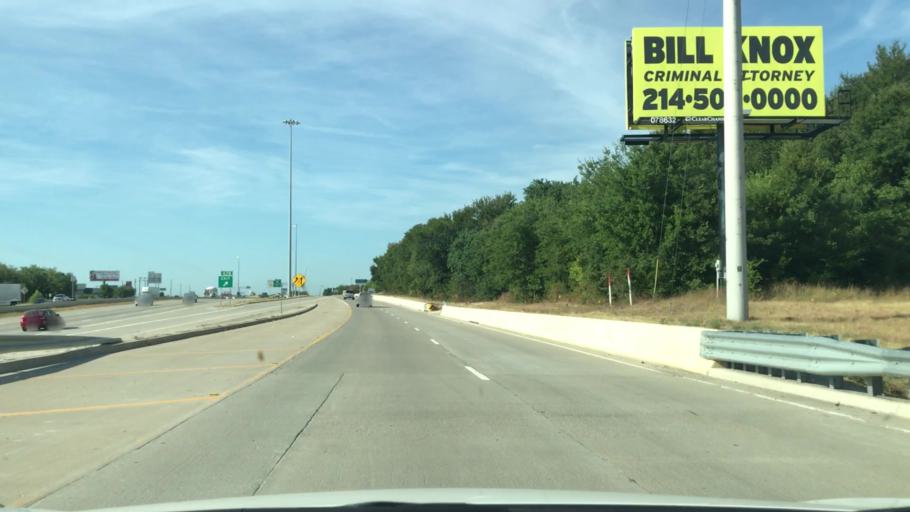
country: US
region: Texas
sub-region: Collin County
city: McKinney
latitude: 33.2384
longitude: -96.6309
